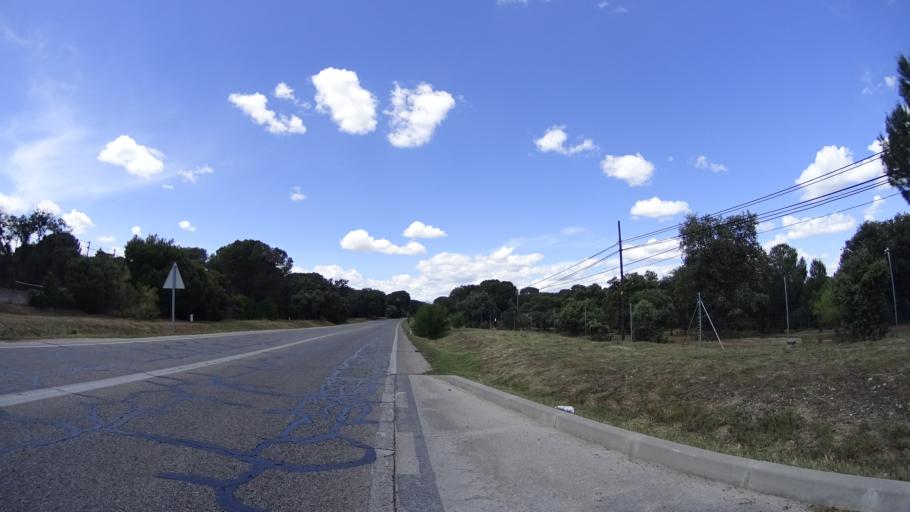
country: ES
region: Madrid
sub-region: Provincia de Madrid
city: Boadilla del Monte
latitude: 40.4300
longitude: -3.8702
